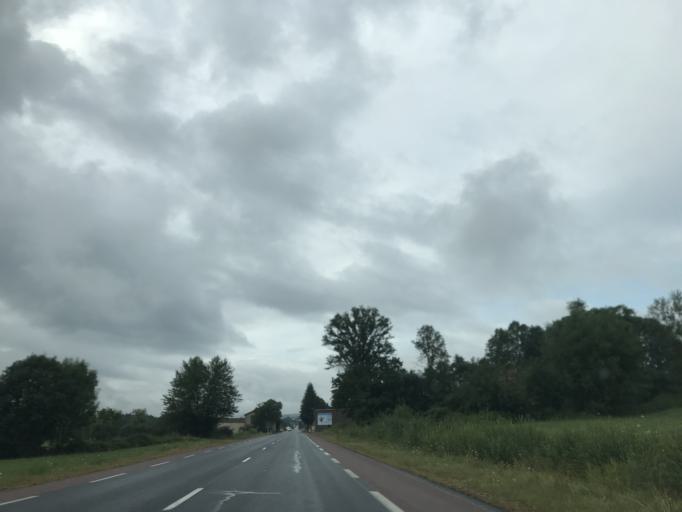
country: FR
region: Auvergne
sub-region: Departement du Puy-de-Dome
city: Arlanc
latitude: 45.4363
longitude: 3.7241
